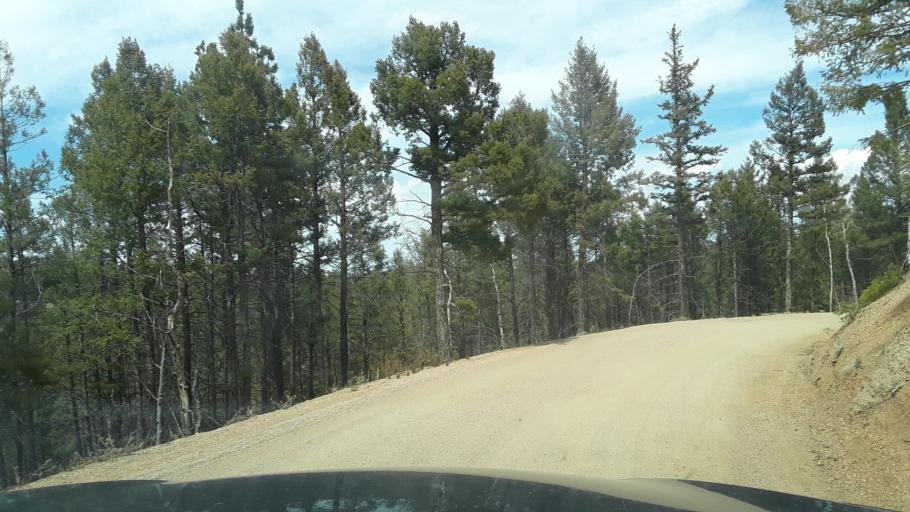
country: US
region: Colorado
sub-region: El Paso County
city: Palmer Lake
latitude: 39.0645
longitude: -104.9710
